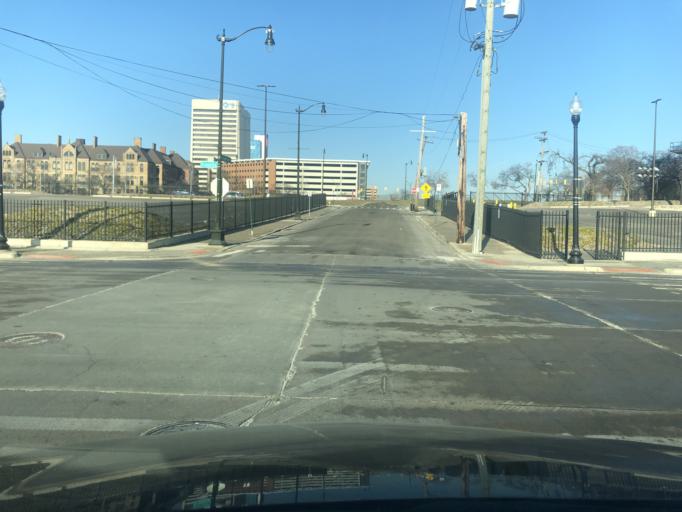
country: US
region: Michigan
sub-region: Wayne County
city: Detroit
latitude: 42.3309
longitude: -83.0353
